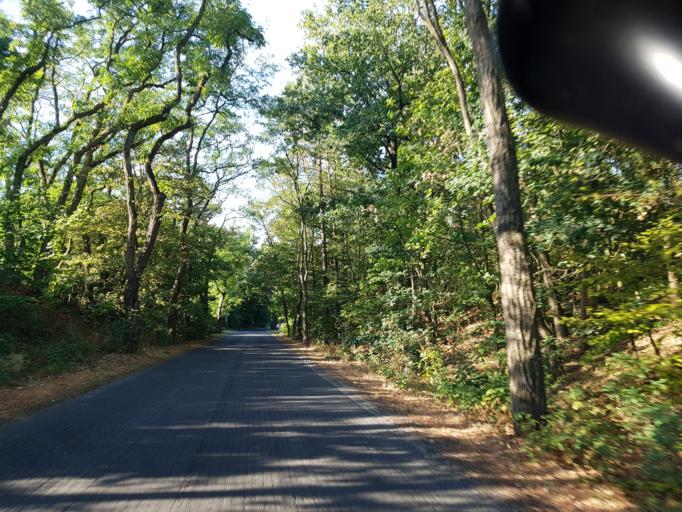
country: DE
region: Brandenburg
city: Elsterwerda
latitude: 51.4772
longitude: 13.5054
